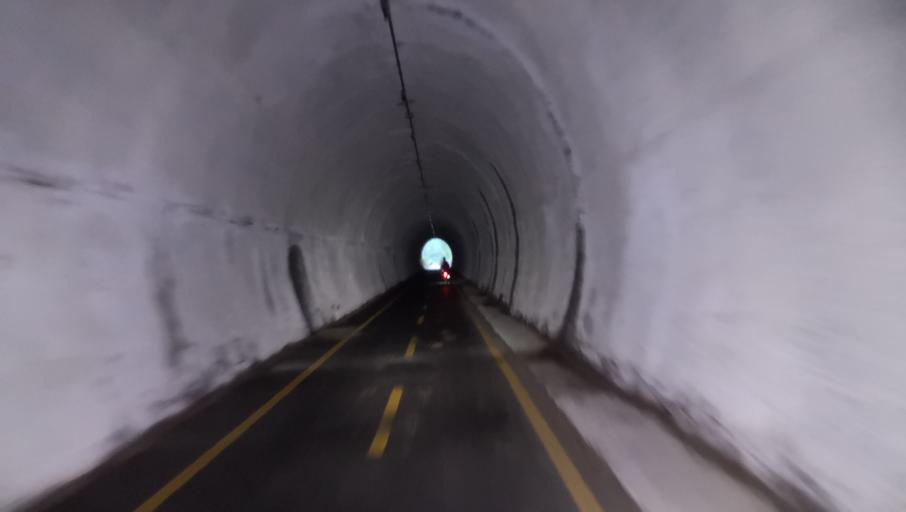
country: IT
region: Friuli Venezia Giulia
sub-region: Provincia di Udine
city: Chiusaforte
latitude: 46.4047
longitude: 13.2915
